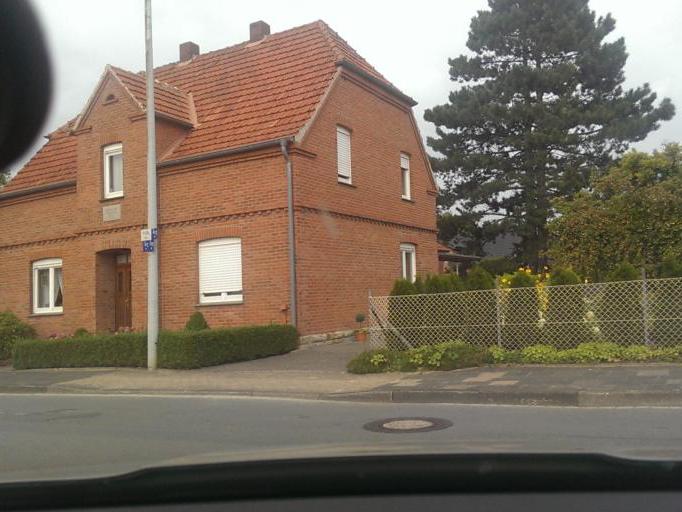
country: DE
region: North Rhine-Westphalia
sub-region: Regierungsbezirk Detmold
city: Delbruck
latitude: 51.7710
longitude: 8.5566
